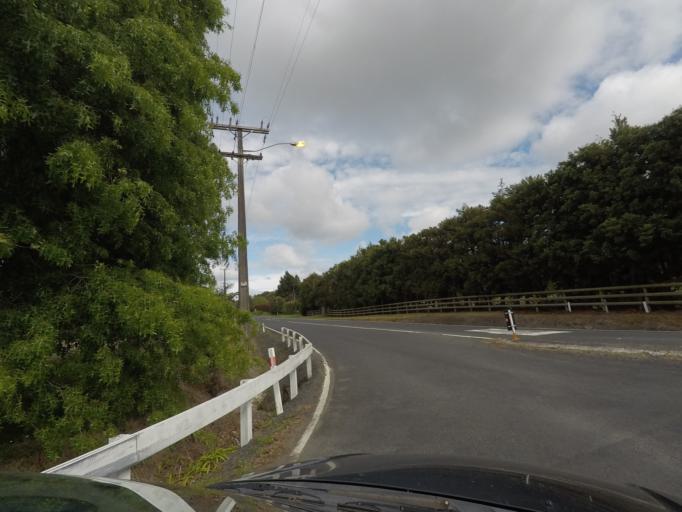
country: NZ
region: Auckland
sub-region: Auckland
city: Rosebank
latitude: -36.7749
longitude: 174.5872
